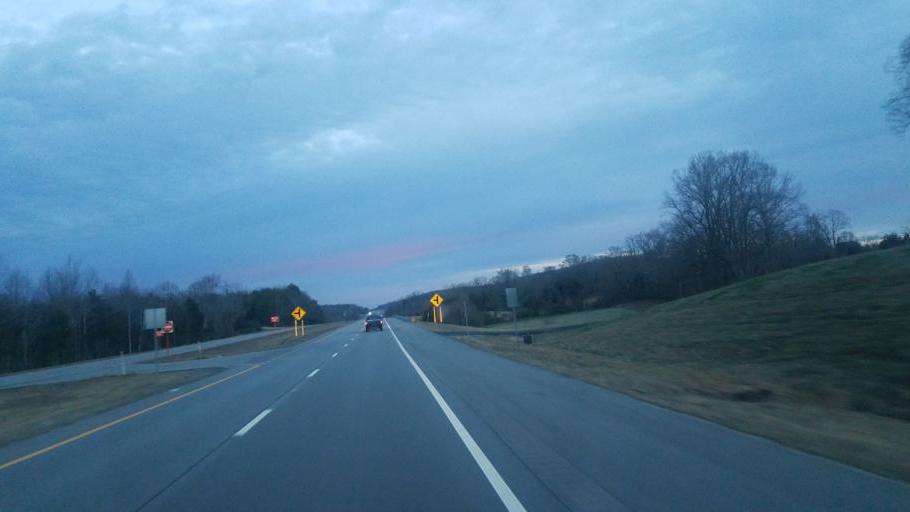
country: US
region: Tennessee
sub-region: Van Buren County
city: Spencer
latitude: 35.8129
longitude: -85.4596
